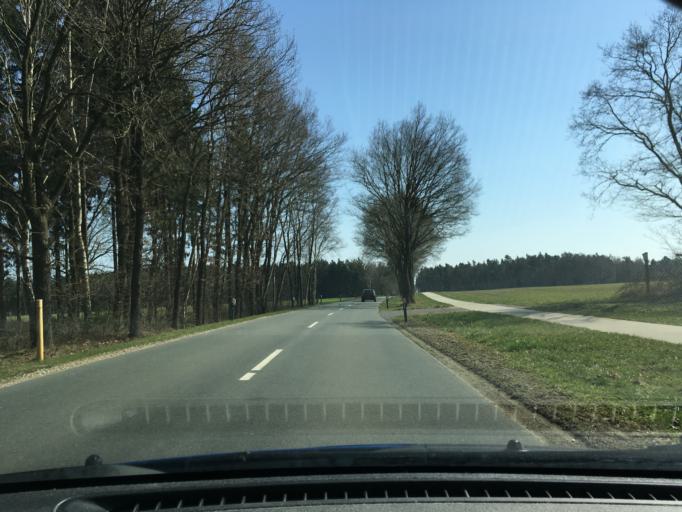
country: DE
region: Lower Saxony
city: Eimke
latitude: 52.9957
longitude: 10.3018
